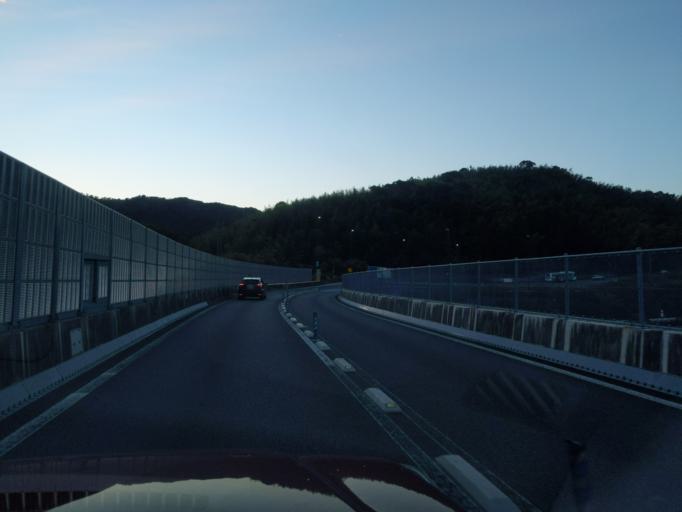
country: JP
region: Tokushima
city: Anan
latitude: 33.8020
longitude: 134.5930
